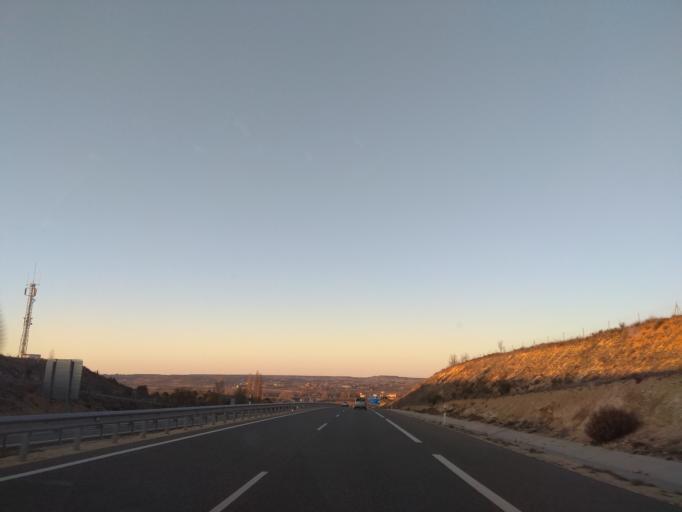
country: ES
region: Castille and Leon
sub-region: Provincia de Burgos
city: Villanueva de Gumiel
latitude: 41.7375
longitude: -3.6883
